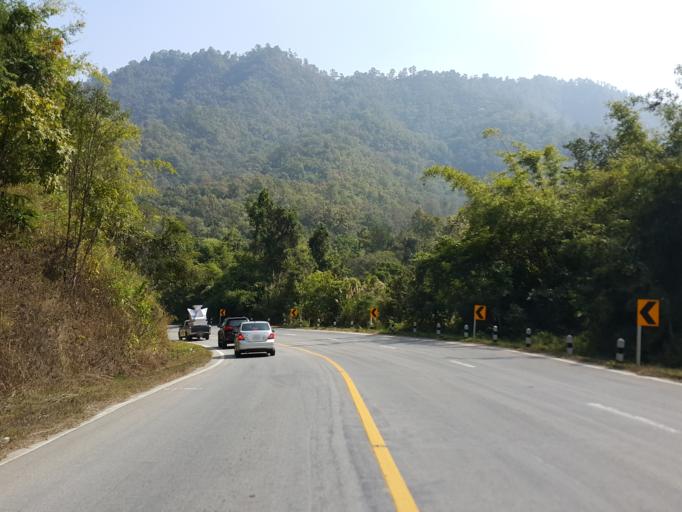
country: TH
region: Lampang
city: Wang Nuea
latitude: 19.0943
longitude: 99.4305
